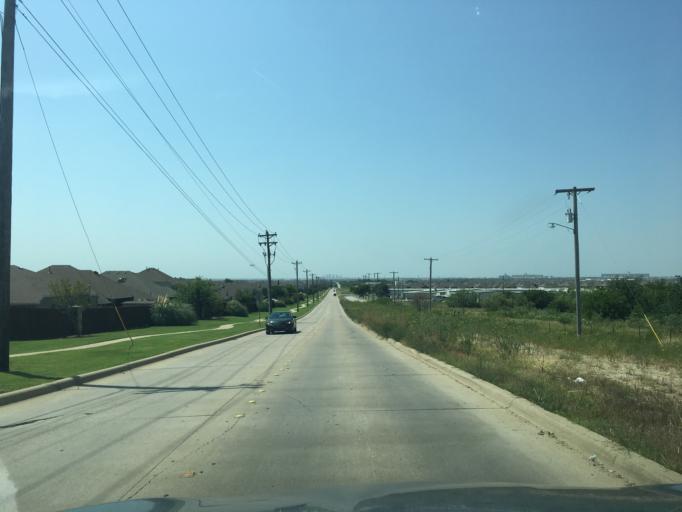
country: US
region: Texas
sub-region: Tarrant County
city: Haslet
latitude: 32.9238
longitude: -97.3315
